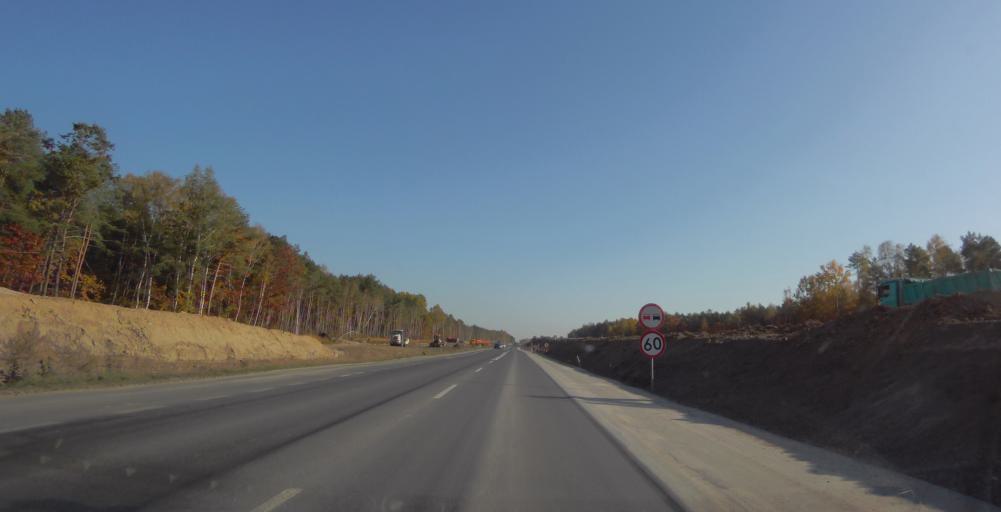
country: PL
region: Masovian Voivodeship
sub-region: Powiat otwocki
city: Celestynow
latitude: 52.0868
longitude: 21.4276
